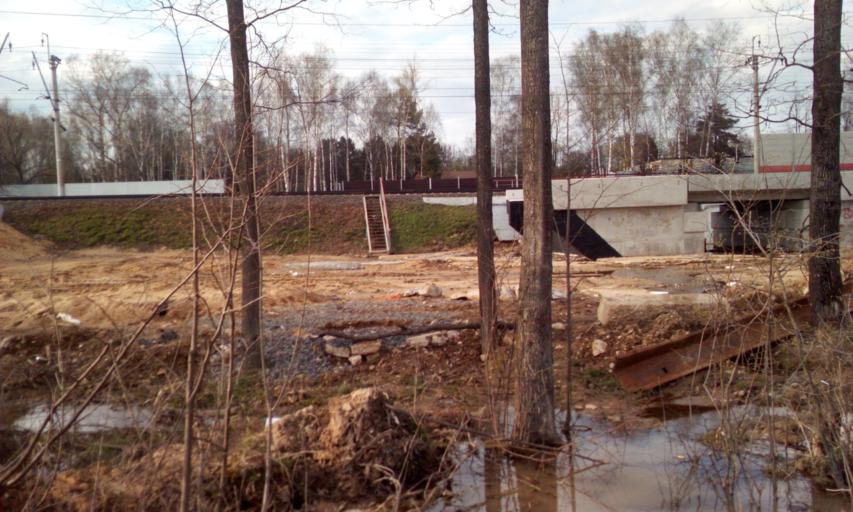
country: RU
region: Moscow
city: Novo-Peredelkino
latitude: 55.6460
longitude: 37.3236
